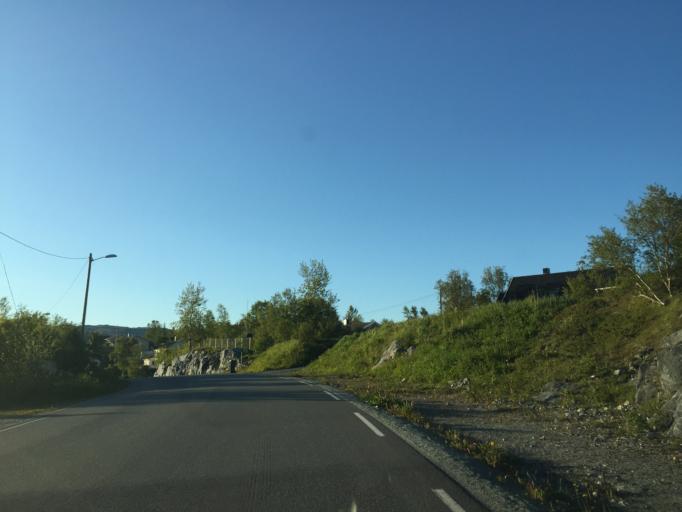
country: NO
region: Nordland
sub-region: Bodo
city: Loding
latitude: 67.2846
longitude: 14.7307
